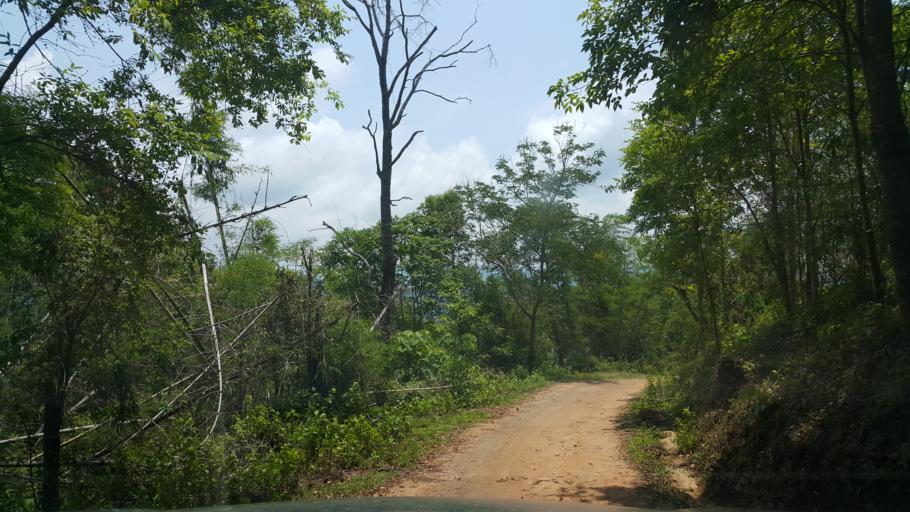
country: TH
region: Chiang Rai
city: Chiang Rai
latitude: 20.0009
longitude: 99.7055
